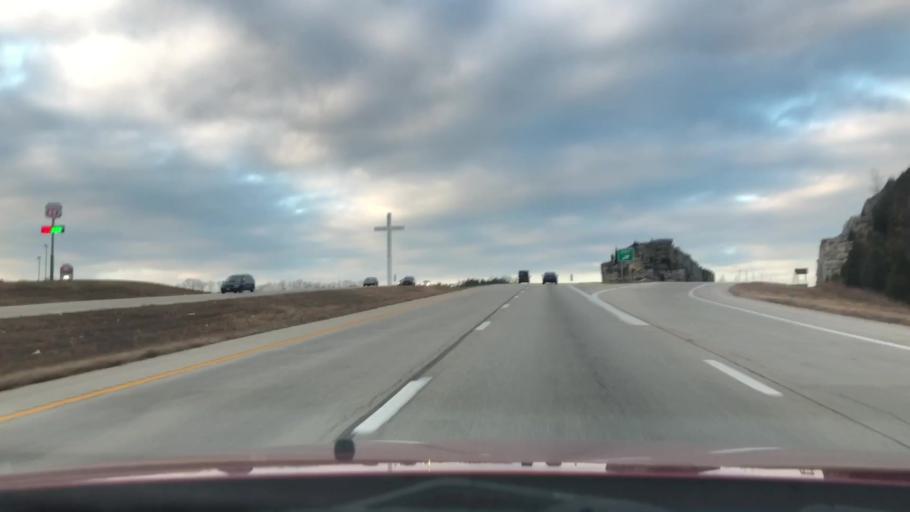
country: US
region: Missouri
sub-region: Taney County
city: Merriam Woods
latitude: 36.7454
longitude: -93.2224
